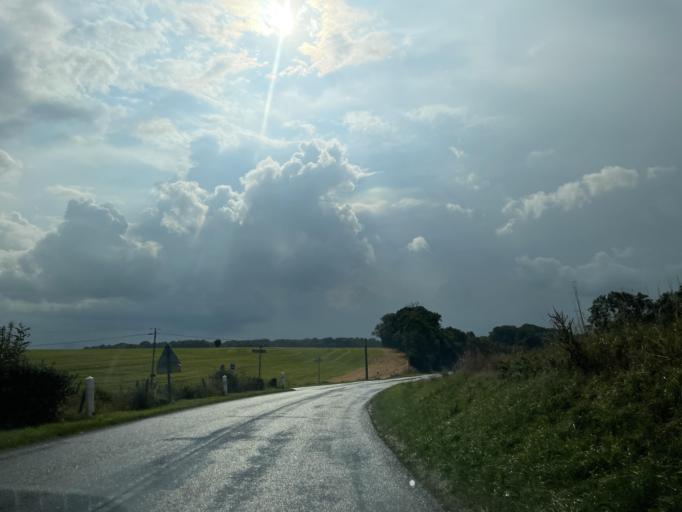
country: FR
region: Haute-Normandie
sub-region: Departement de la Seine-Maritime
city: Envermeu
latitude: 49.9098
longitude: 1.2769
